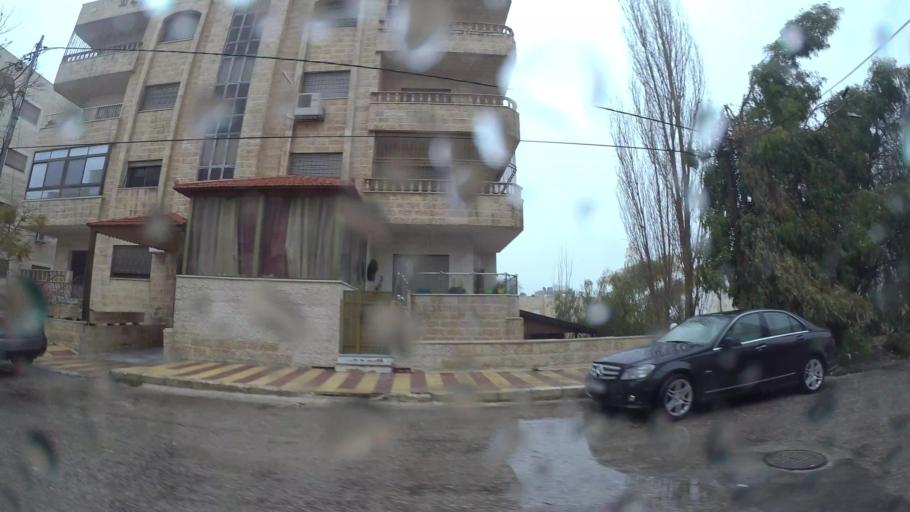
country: JO
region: Amman
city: Al Jubayhah
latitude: 32.0096
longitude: 35.8867
